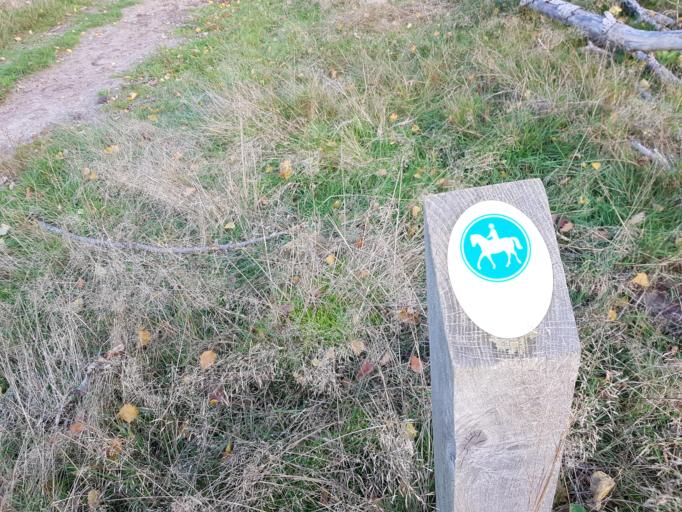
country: NL
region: North Holland
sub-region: Gemeente Hilversum
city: Hilversum
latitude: 52.2000
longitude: 5.2262
